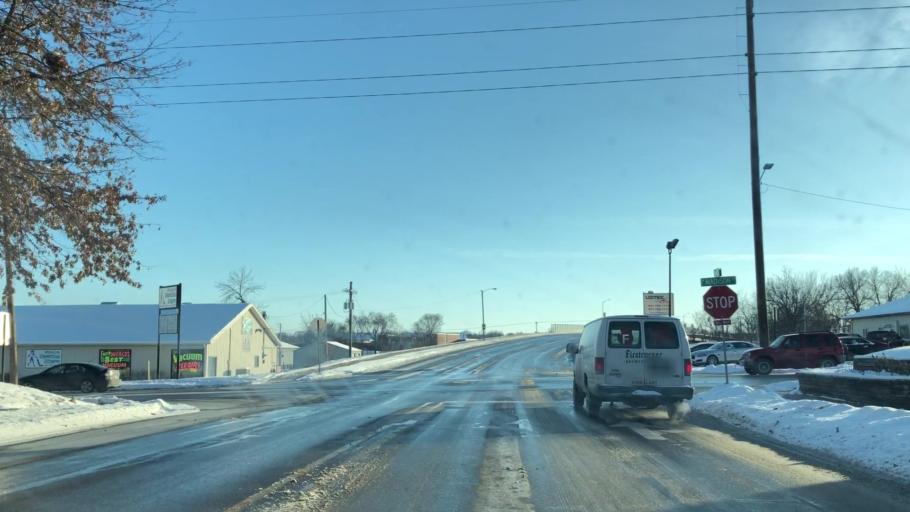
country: US
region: Iowa
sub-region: Marshall County
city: Marshalltown
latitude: 42.0433
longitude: -92.9179
